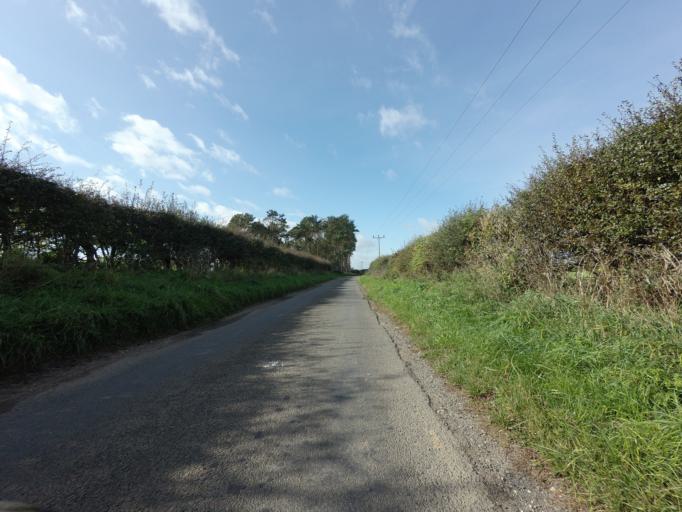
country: GB
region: England
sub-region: Norfolk
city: Hunstanton
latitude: 52.9363
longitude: 0.6357
